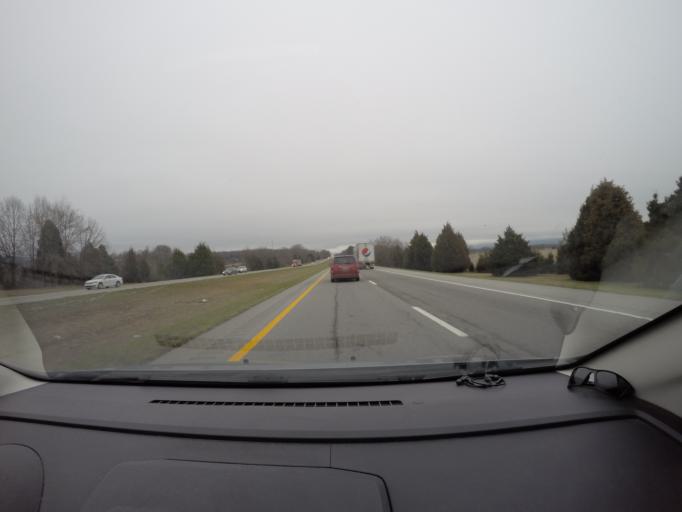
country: US
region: Tennessee
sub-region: Franklin County
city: Sewanee
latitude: 35.3461
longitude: -85.9449
